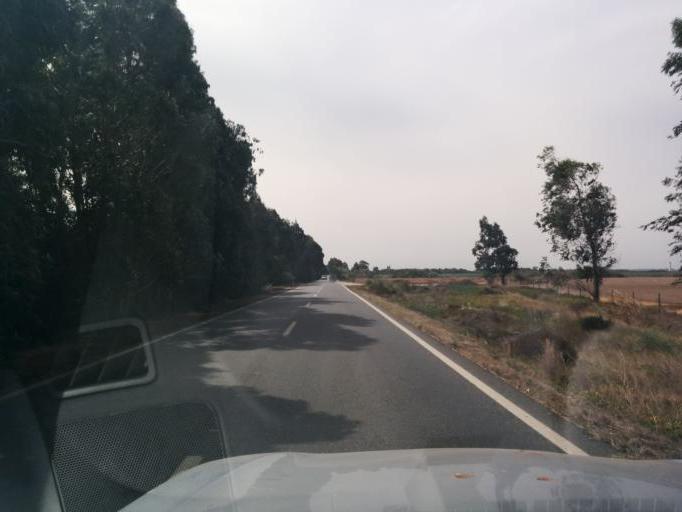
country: PT
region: Beja
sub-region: Odemira
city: Vila Nova de Milfontes
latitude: 37.6878
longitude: -8.7658
